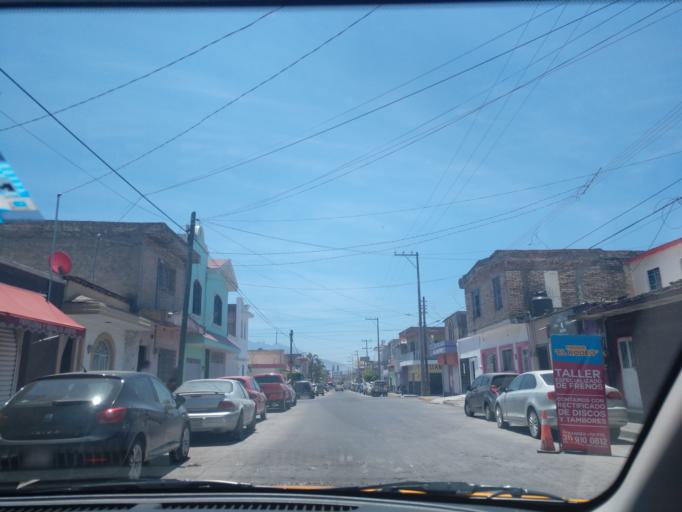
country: MX
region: Nayarit
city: Tepic
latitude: 21.5190
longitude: -104.9032
